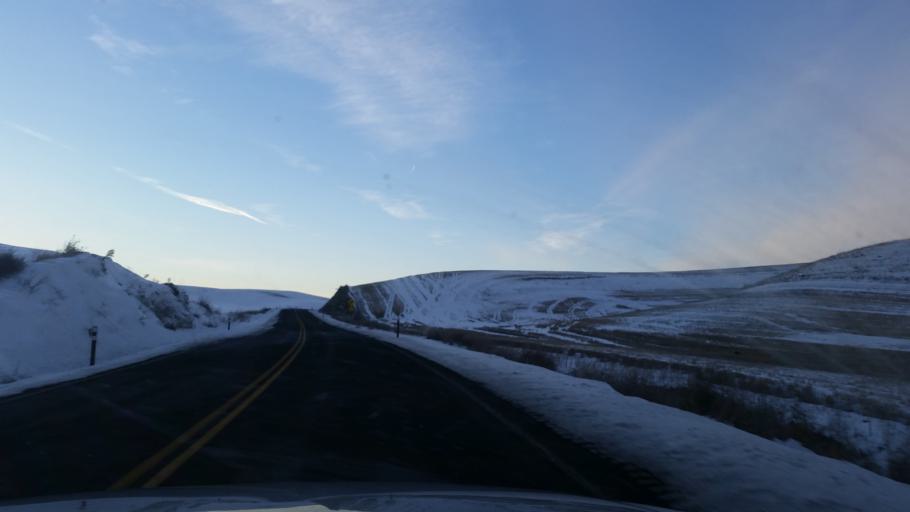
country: US
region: Washington
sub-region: Spokane County
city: Cheney
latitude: 47.1549
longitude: -117.8471
